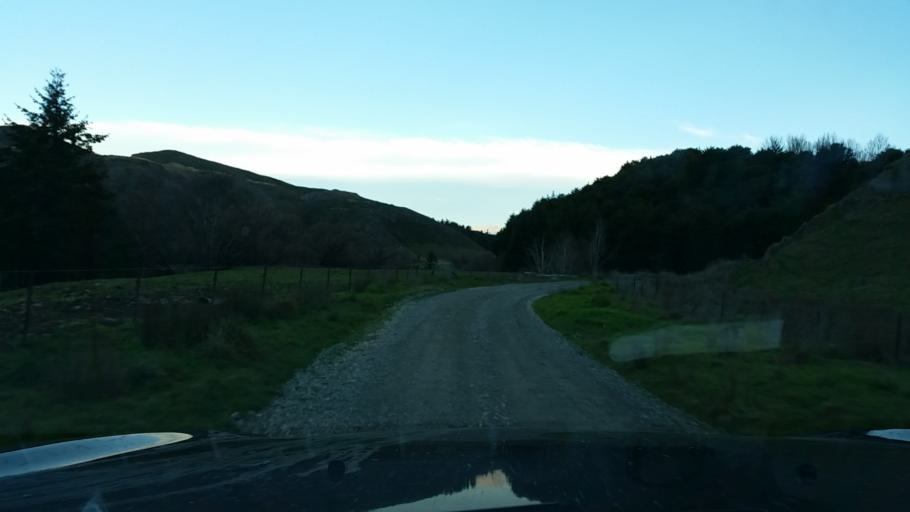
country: NZ
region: Marlborough
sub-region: Marlborough District
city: Blenheim
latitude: -41.5034
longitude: 173.5898
